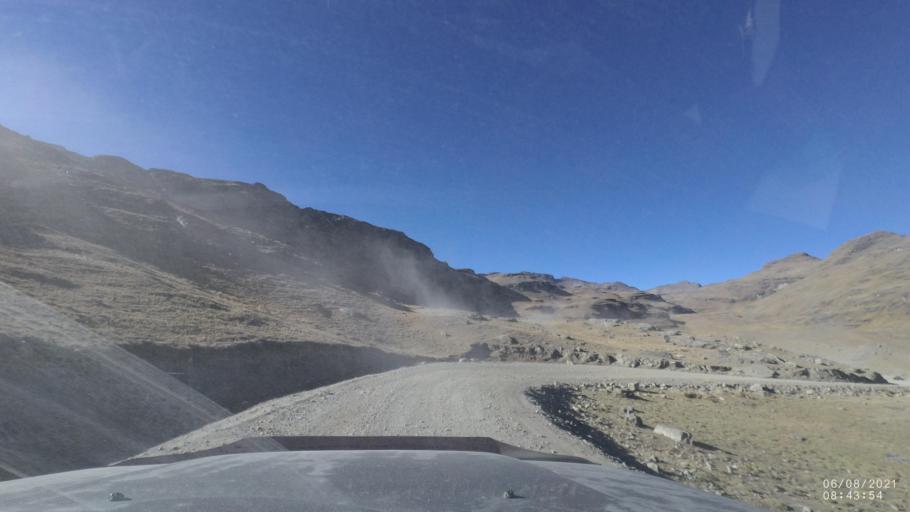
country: BO
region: Cochabamba
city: Sipe Sipe
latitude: -17.1706
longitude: -66.4093
